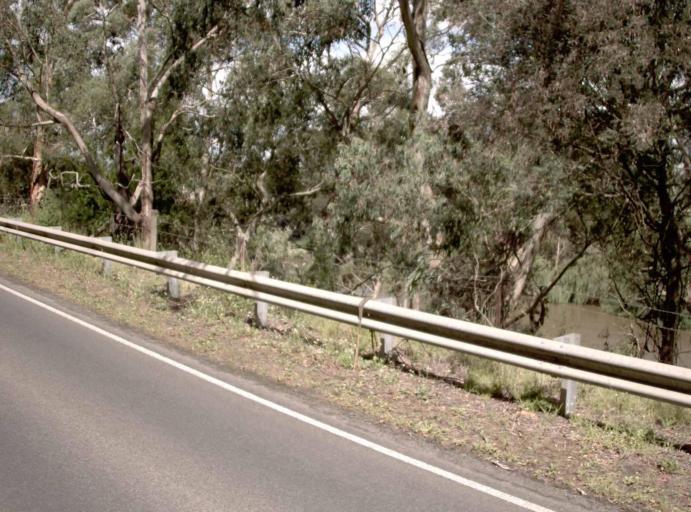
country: AU
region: Victoria
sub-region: Latrobe
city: Morwell
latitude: -38.1717
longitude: 146.3489
